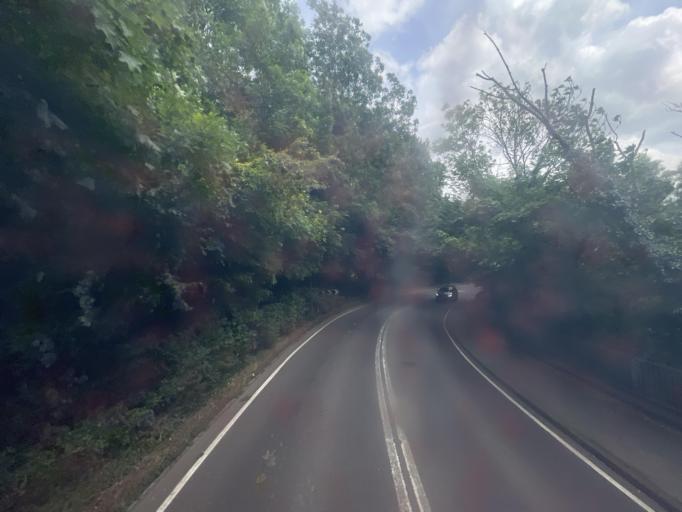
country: GB
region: England
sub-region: Kent
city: Biggin Hill
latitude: 51.3508
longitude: 0.0348
